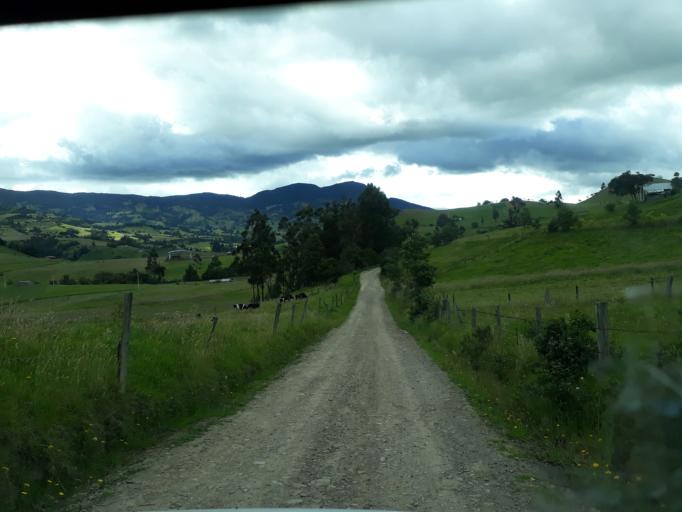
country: CO
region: Cundinamarca
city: La Mesa
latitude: 5.2683
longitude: -73.8994
